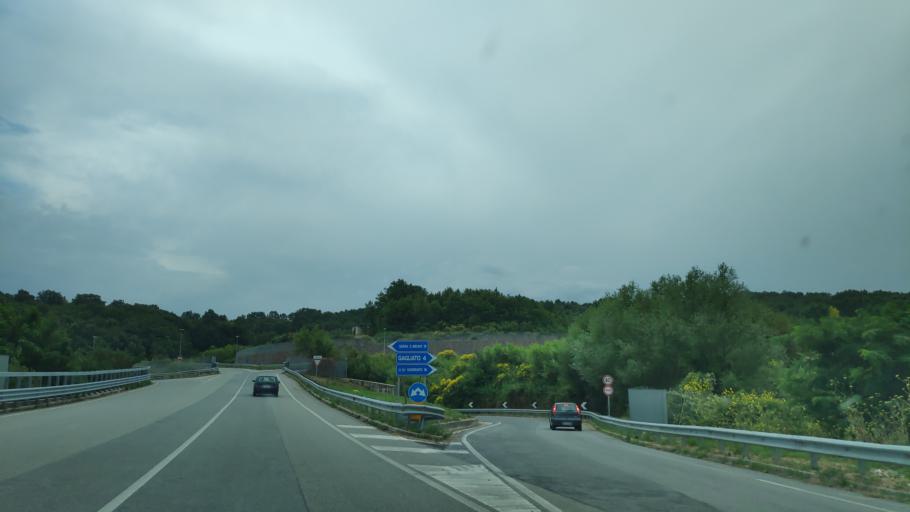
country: IT
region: Calabria
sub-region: Provincia di Catanzaro
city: Argusto
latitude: 38.6817
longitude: 16.4247
